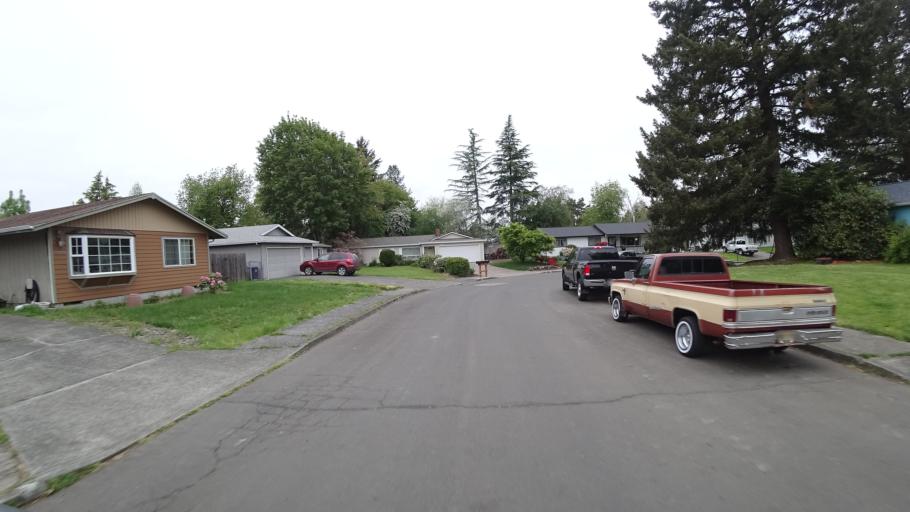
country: US
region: Oregon
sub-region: Washington County
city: Aloha
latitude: 45.5050
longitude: -122.8834
